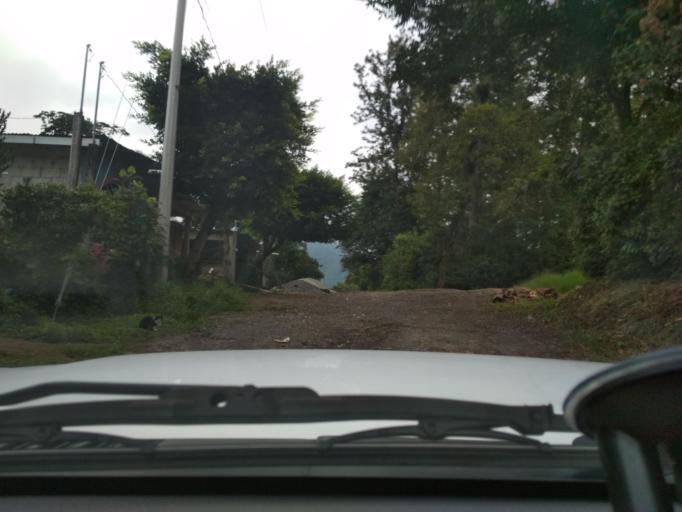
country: MX
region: Veracruz
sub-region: Ixtaczoquitlan
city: Buenavista
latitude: 18.9117
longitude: -97.0515
